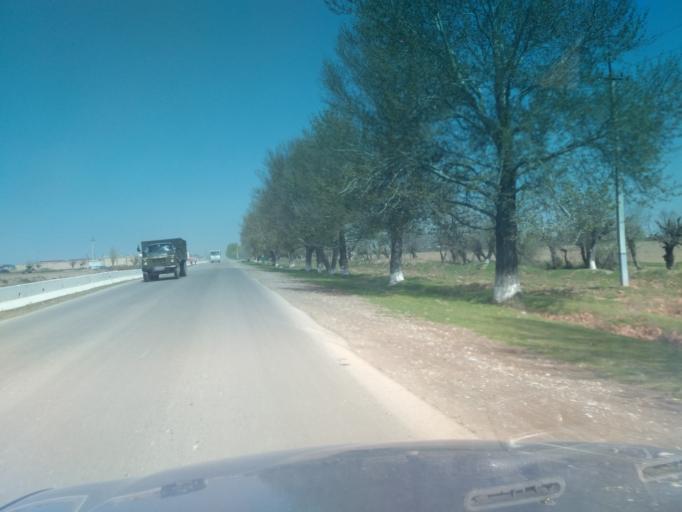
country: UZ
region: Sirdaryo
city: Guliston
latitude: 40.5028
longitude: 68.7978
